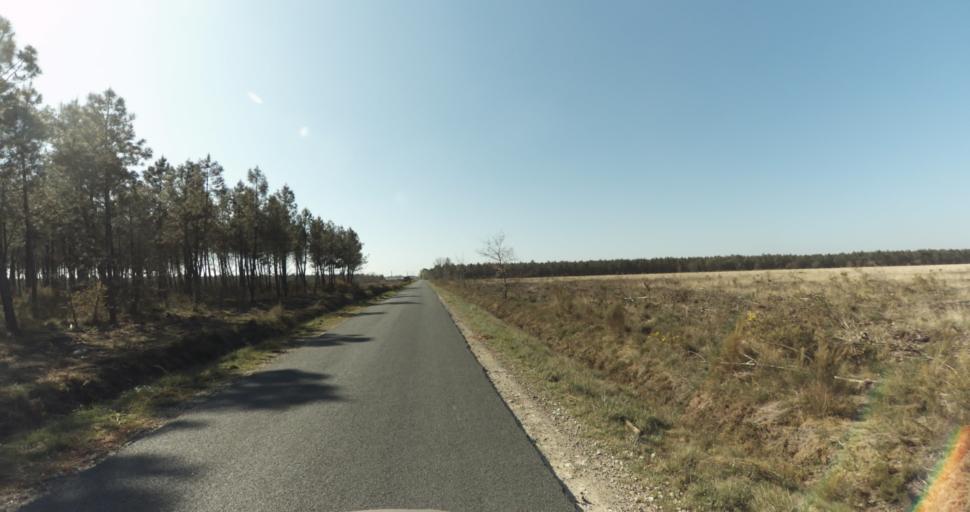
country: FR
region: Aquitaine
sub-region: Departement de la Gironde
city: Marcheprime
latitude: 44.7796
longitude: -0.8602
